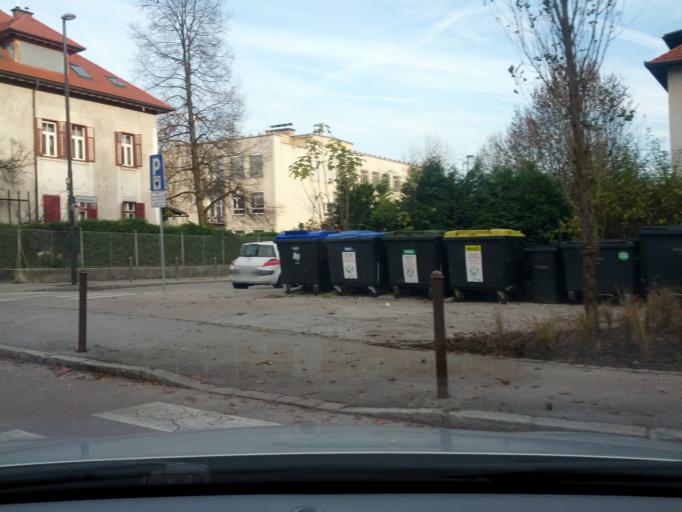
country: SI
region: Ljubljana
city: Ljubljana
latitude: 46.0471
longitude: 14.5149
